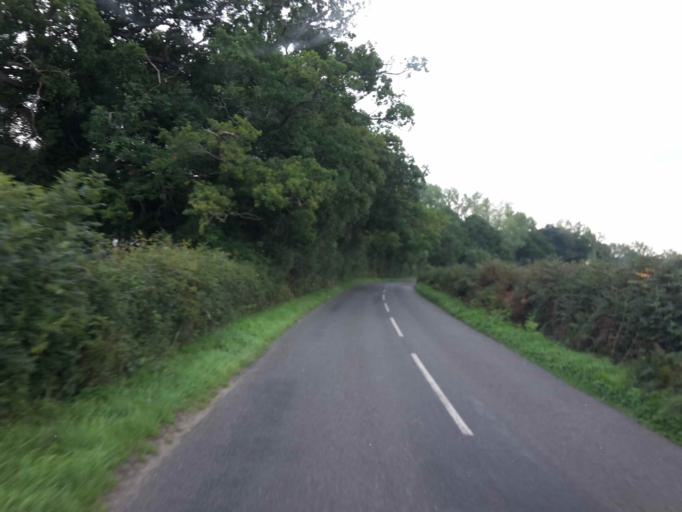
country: GB
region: England
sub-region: West Sussex
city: Rudgwick
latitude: 51.0695
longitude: -0.4485
